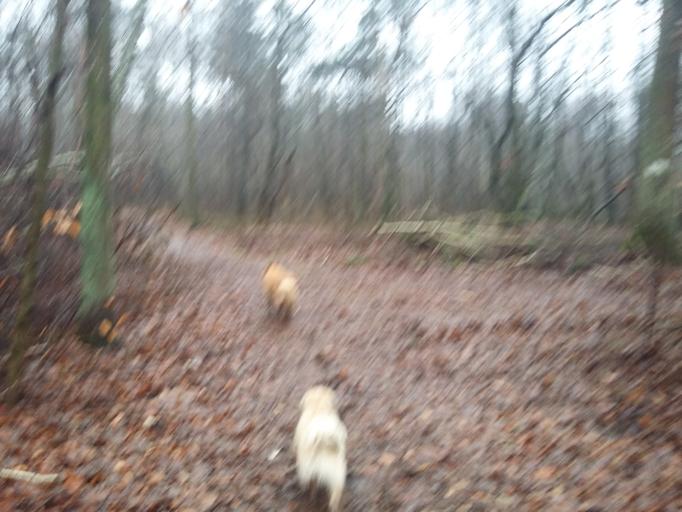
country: PL
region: Lodz Voivodeship
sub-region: Powiat pabianicki
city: Ksawerow
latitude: 51.7255
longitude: 19.3753
